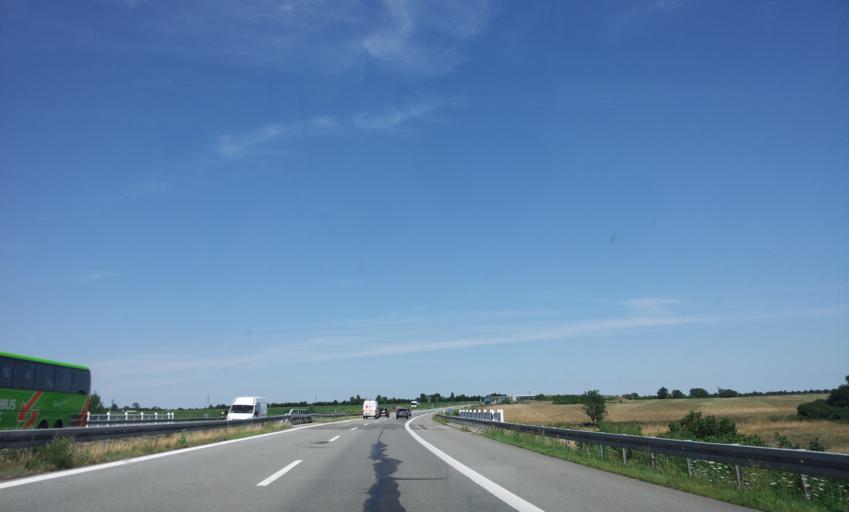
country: DE
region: Mecklenburg-Vorpommern
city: Jarmen
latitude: 53.8961
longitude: 13.3421
